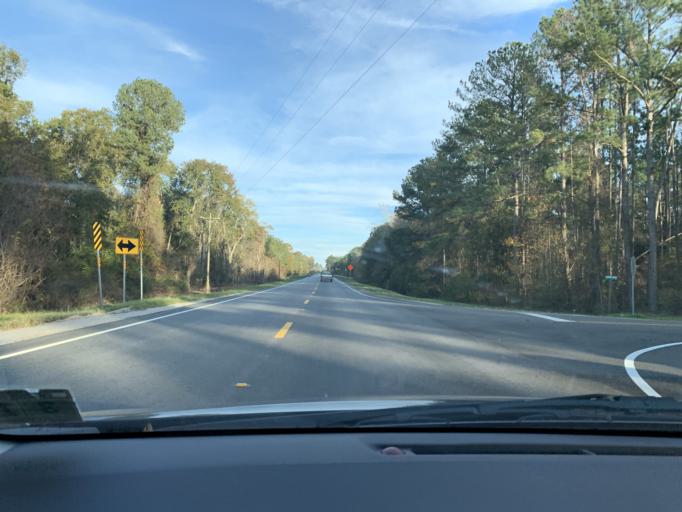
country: US
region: Georgia
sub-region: Irwin County
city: Ocilla
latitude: 31.5960
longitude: -83.1742
